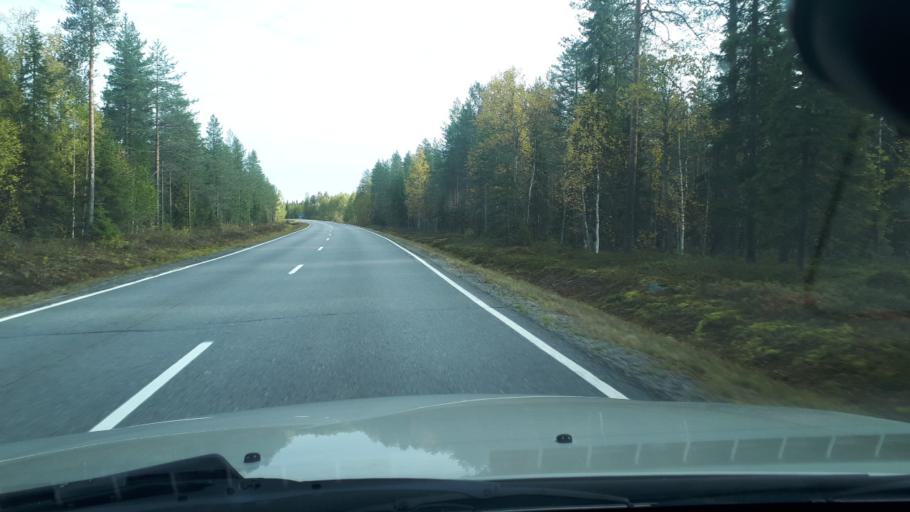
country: FI
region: Northern Ostrobothnia
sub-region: Oulu
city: Yli-Ii
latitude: 65.9293
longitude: 25.8598
